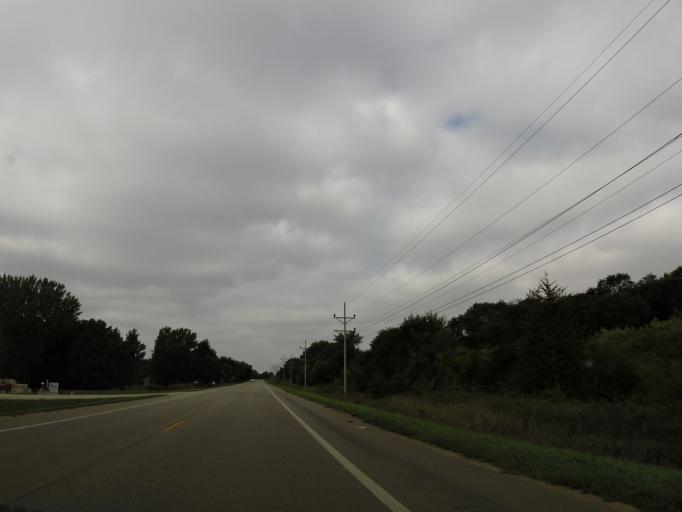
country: US
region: Minnesota
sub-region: Chippewa County
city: Montevideo
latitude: 44.9194
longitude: -95.6979
